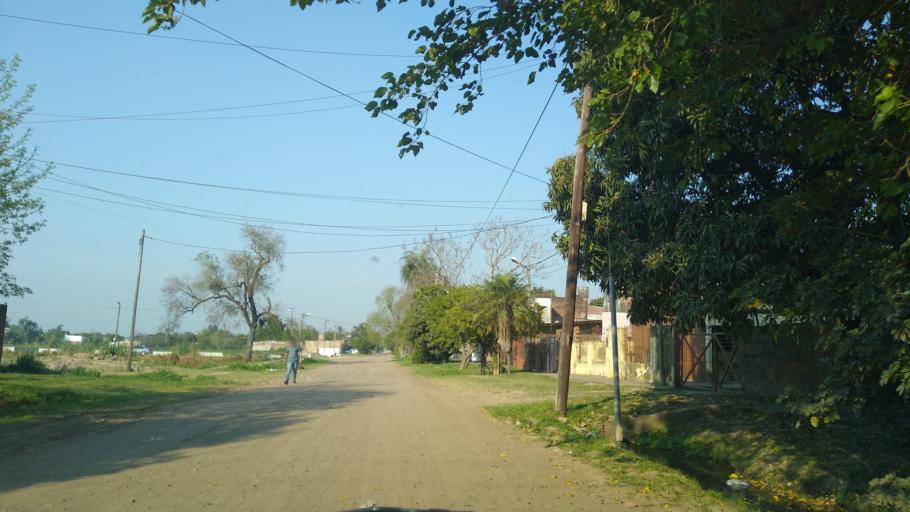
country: AR
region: Chaco
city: Barranqueras
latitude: -27.4797
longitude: -58.9308
